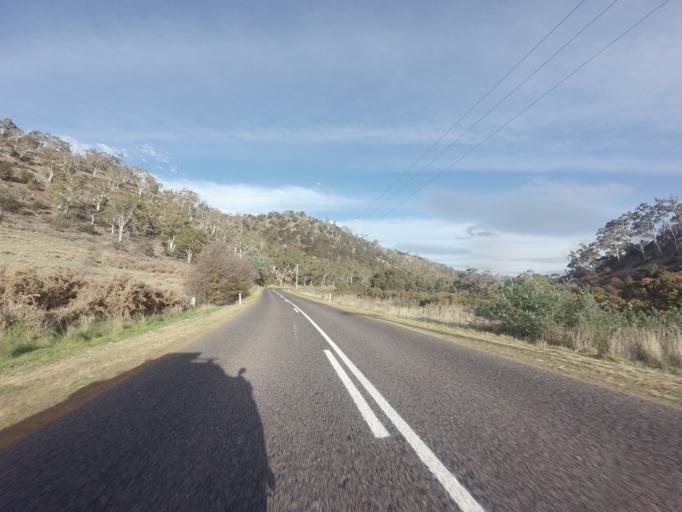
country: AU
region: Tasmania
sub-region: Brighton
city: Bridgewater
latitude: -42.4448
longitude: 147.1527
